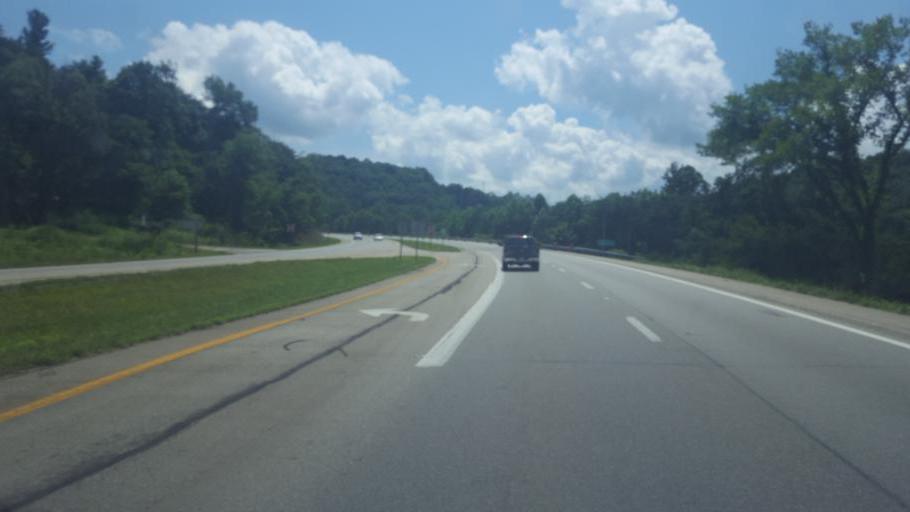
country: US
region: Ohio
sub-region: Jackson County
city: Jackson
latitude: 39.1244
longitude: -82.7007
